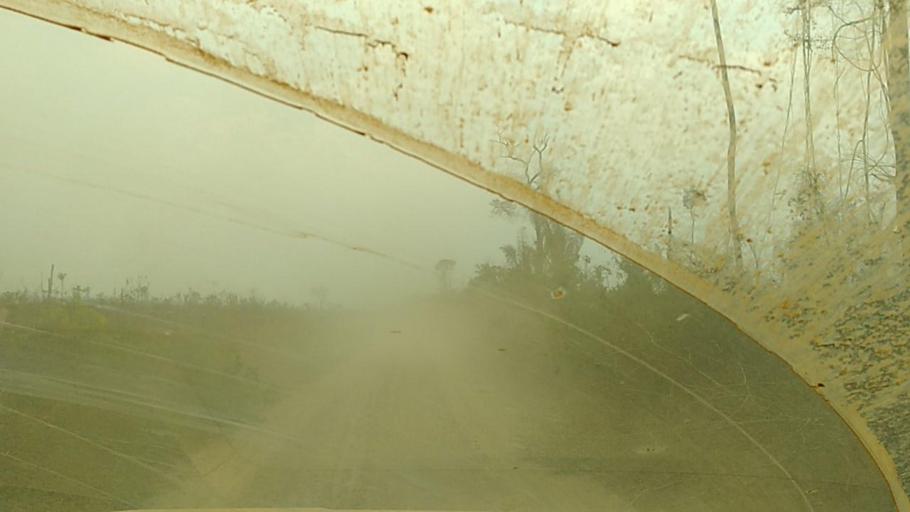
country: BR
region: Rondonia
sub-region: Porto Velho
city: Porto Velho
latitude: -8.7737
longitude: -63.2089
